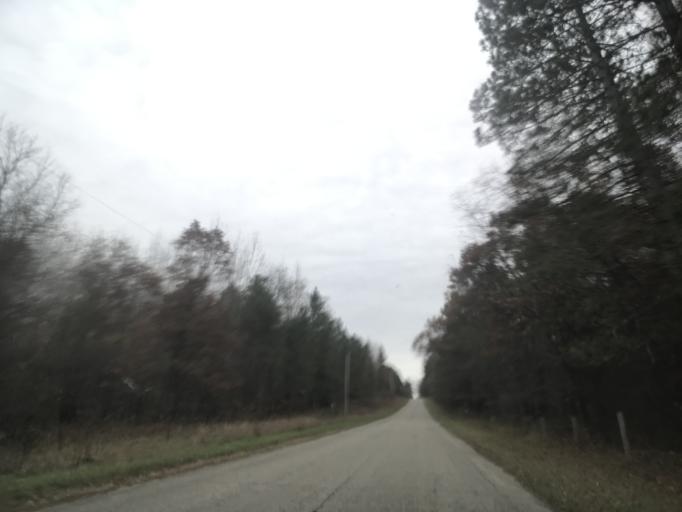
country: US
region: Wisconsin
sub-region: Oconto County
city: Gillett
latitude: 45.3265
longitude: -88.2762
